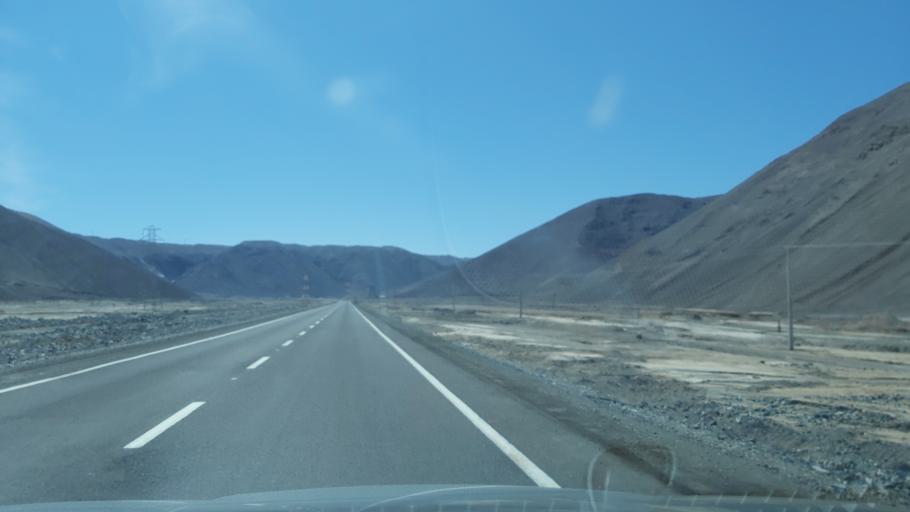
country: CL
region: Atacama
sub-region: Provincia de Chanaral
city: Diego de Almagro
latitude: -26.3314
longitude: -69.8105
